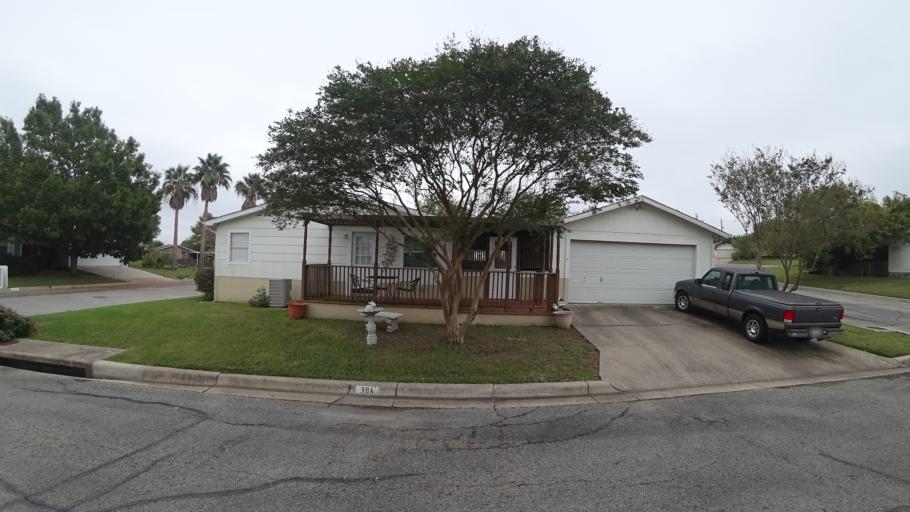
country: US
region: Texas
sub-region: Travis County
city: Pflugerville
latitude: 30.3901
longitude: -97.6441
